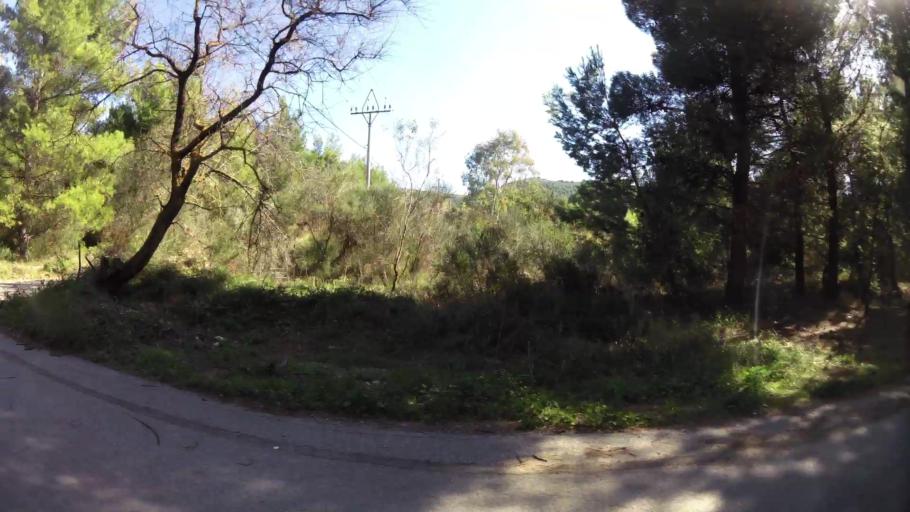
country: GR
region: Attica
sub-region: Nomarchia Athinas
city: Ekali
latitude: 38.1042
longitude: 23.8280
